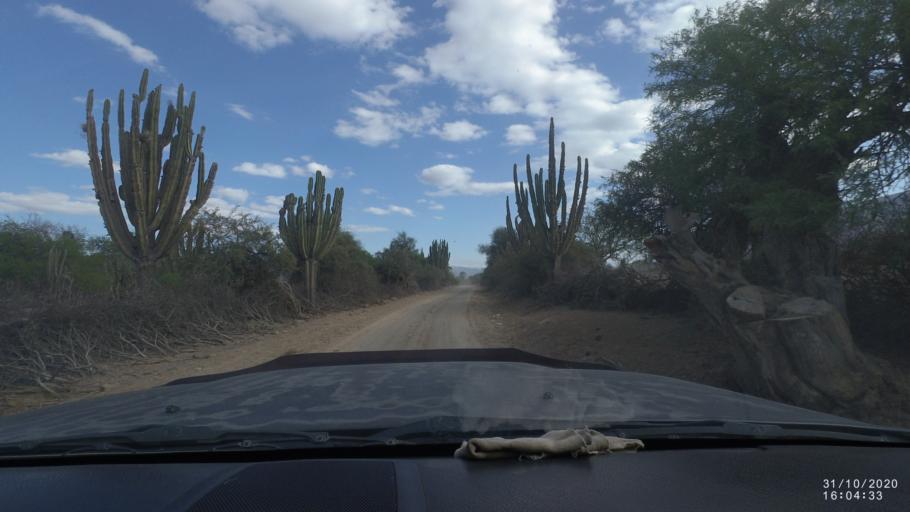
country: BO
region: Chuquisaca
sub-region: Provincia Zudanez
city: Mojocoya
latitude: -18.3601
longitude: -64.6513
